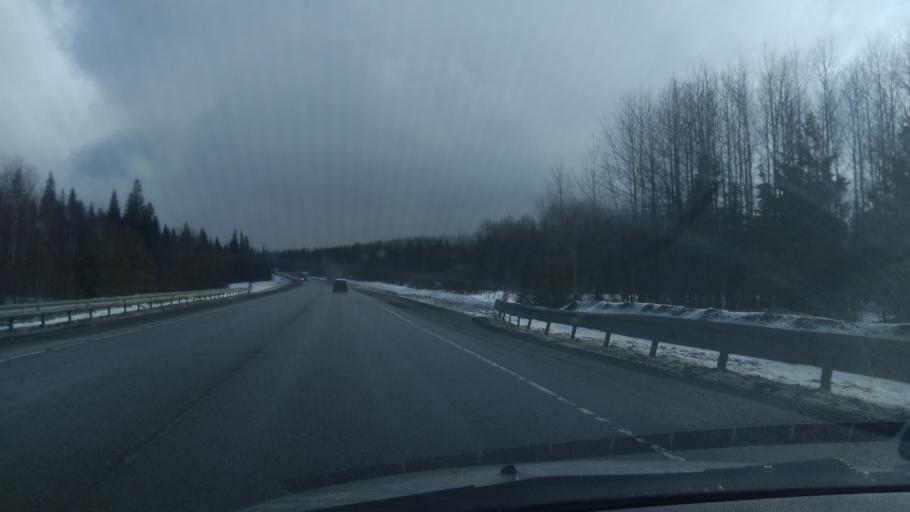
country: RU
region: Sverdlovsk
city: Arti
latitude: 56.7906
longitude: 58.4994
